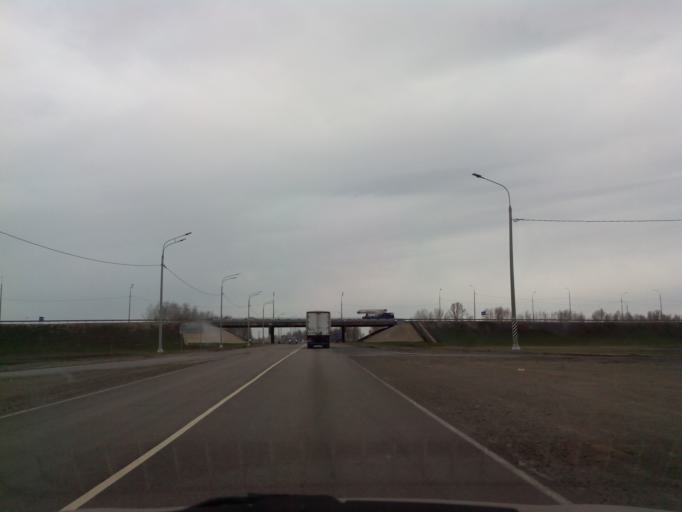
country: RU
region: Tambov
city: Pokrovo-Prigorodnoye
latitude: 52.6594
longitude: 41.3400
